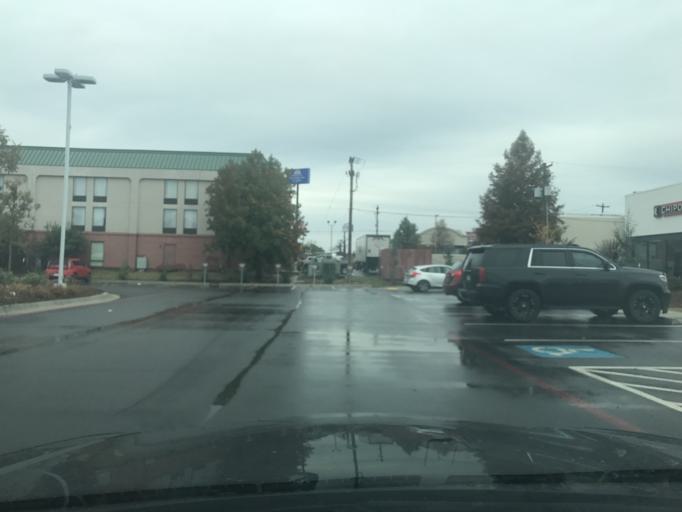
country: US
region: Arkansas
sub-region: Faulkner County
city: Conway
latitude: 35.0908
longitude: -92.4179
